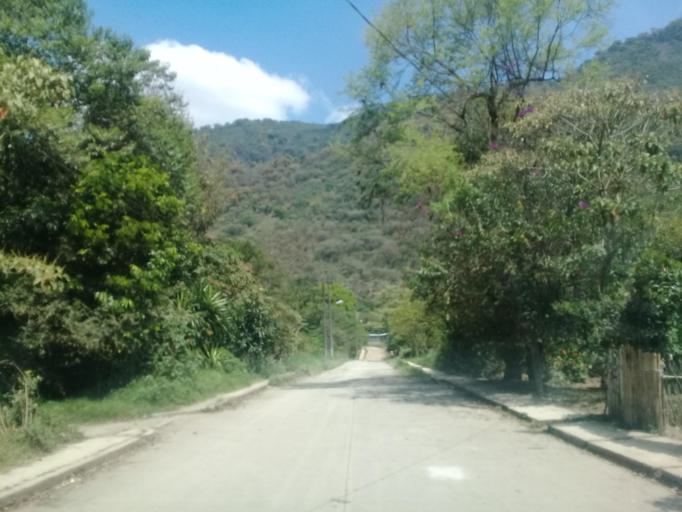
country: MX
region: Veracruz
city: Jalapilla
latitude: 18.8162
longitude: -97.0643
